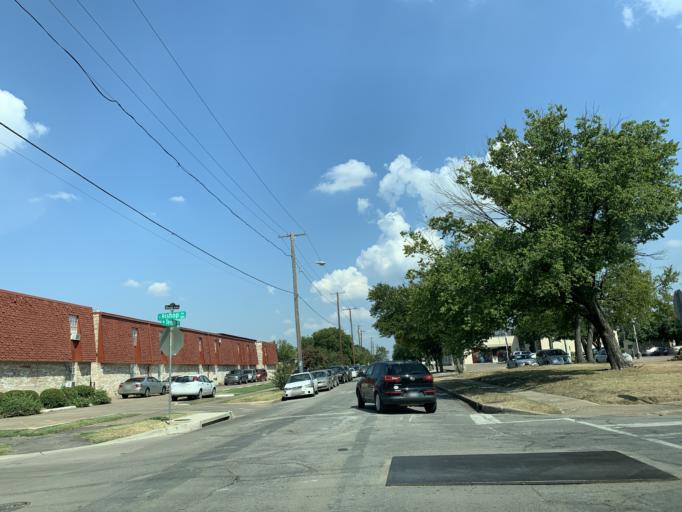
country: US
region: Texas
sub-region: Dallas County
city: Dallas
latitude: 32.7451
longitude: -96.8284
